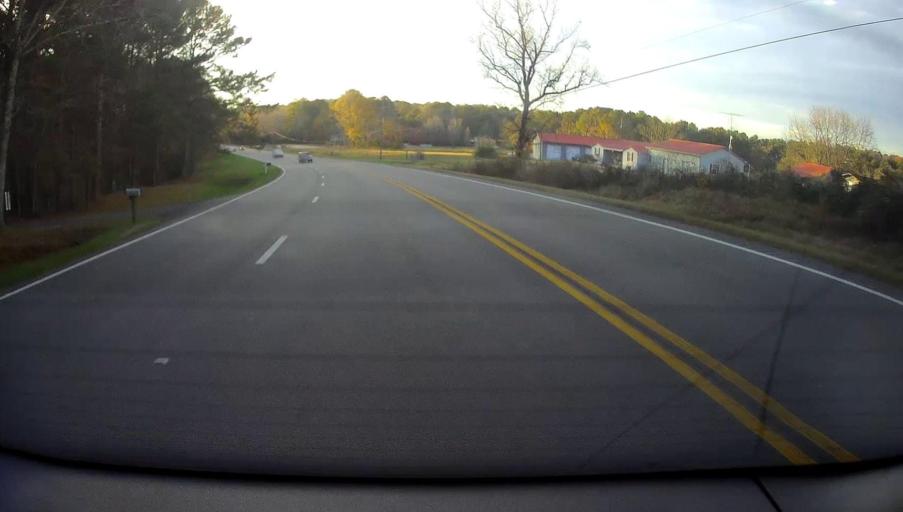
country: US
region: Alabama
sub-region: Saint Clair County
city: Steele
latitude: 34.0667
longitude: -86.2514
